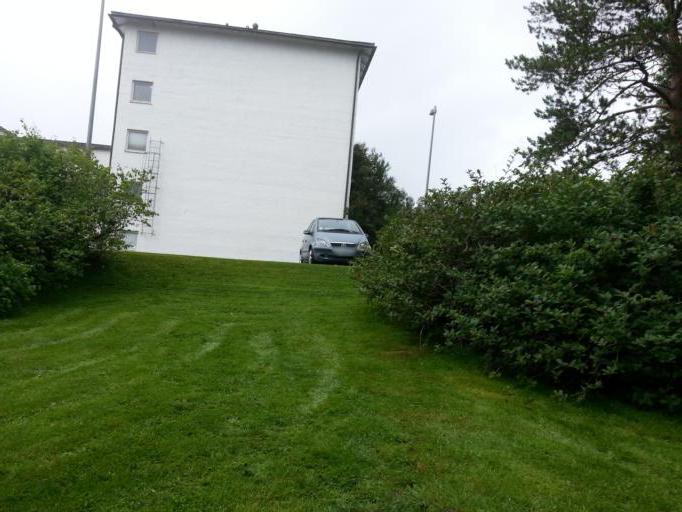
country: NO
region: Troms
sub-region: Tromso
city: Tromso
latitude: 69.6345
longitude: 18.9133
